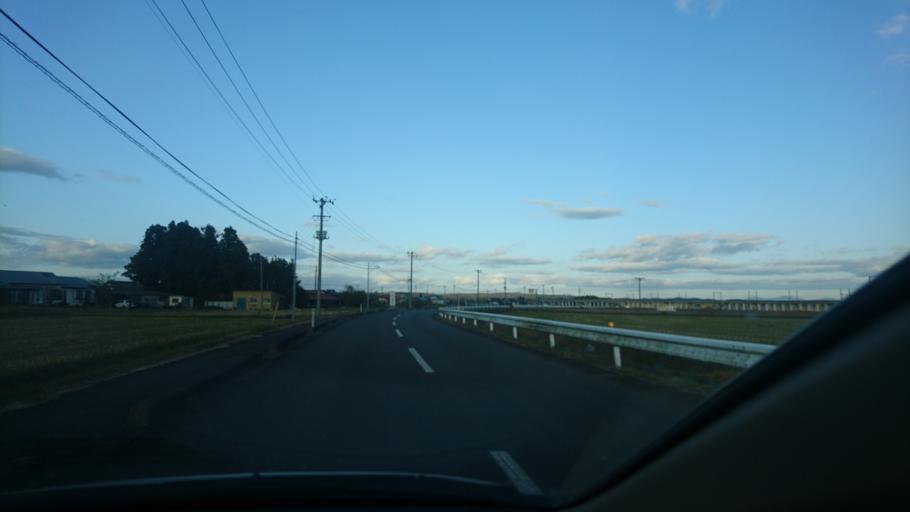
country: JP
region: Iwate
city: Ichinoseki
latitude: 38.7797
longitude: 141.0830
